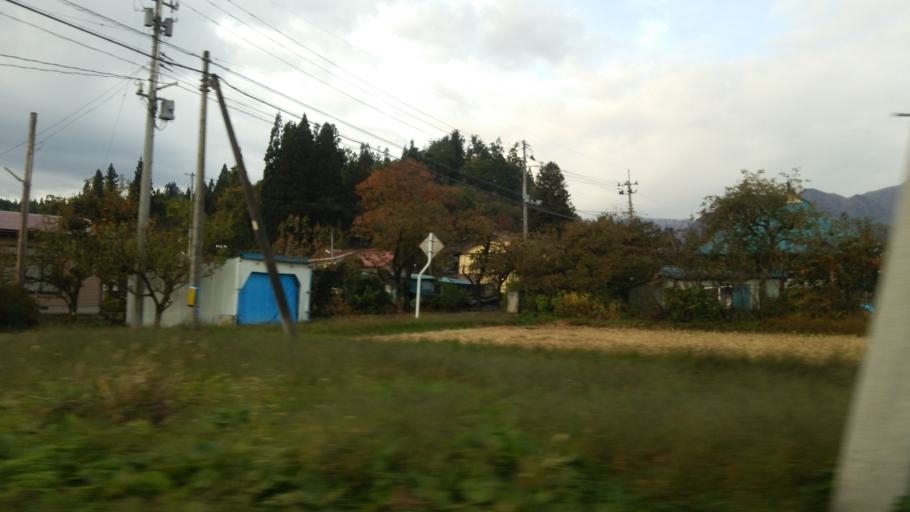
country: JP
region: Fukushima
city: Kitakata
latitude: 37.4341
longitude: 139.8175
